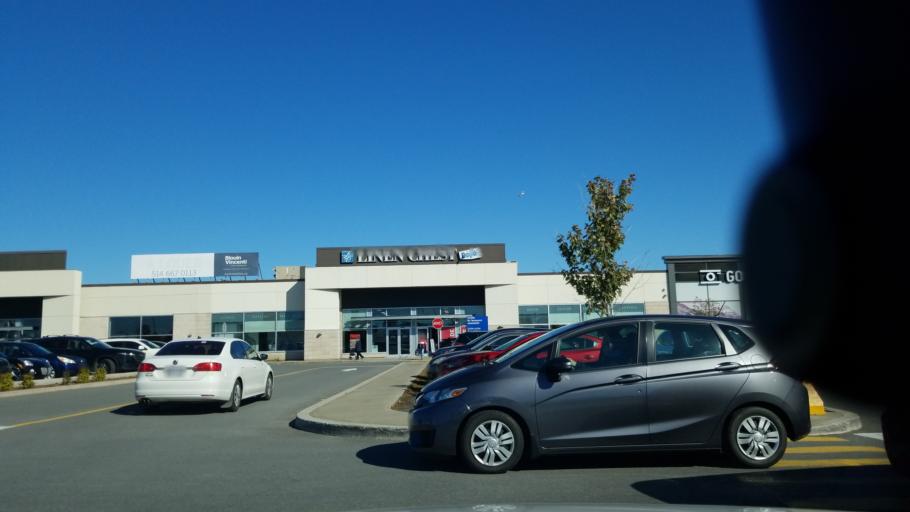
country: CA
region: Quebec
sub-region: Laval
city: Laval
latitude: 45.5644
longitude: -73.7306
